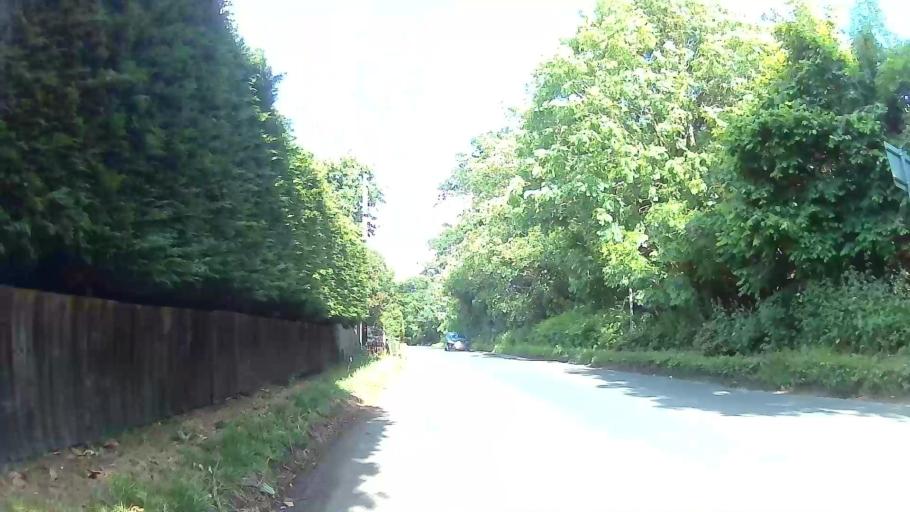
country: GB
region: England
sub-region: Essex
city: Kelvedon Hatch
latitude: 51.6576
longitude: 0.2620
